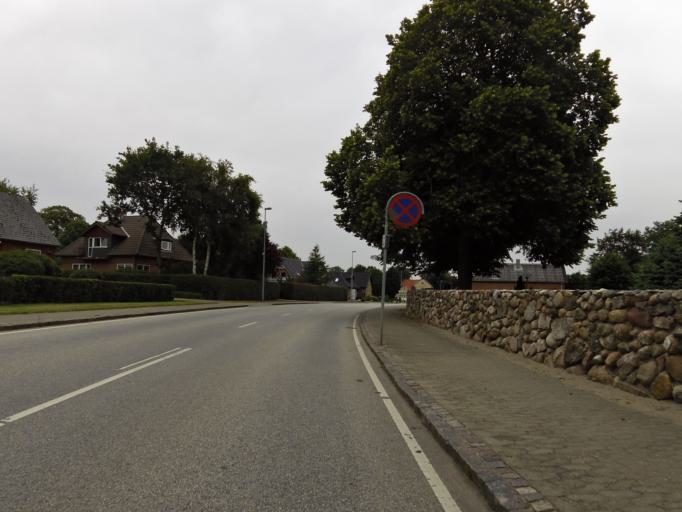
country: DK
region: South Denmark
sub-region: Tonder Kommune
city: Logumkloster
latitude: 55.1489
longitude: 8.9609
